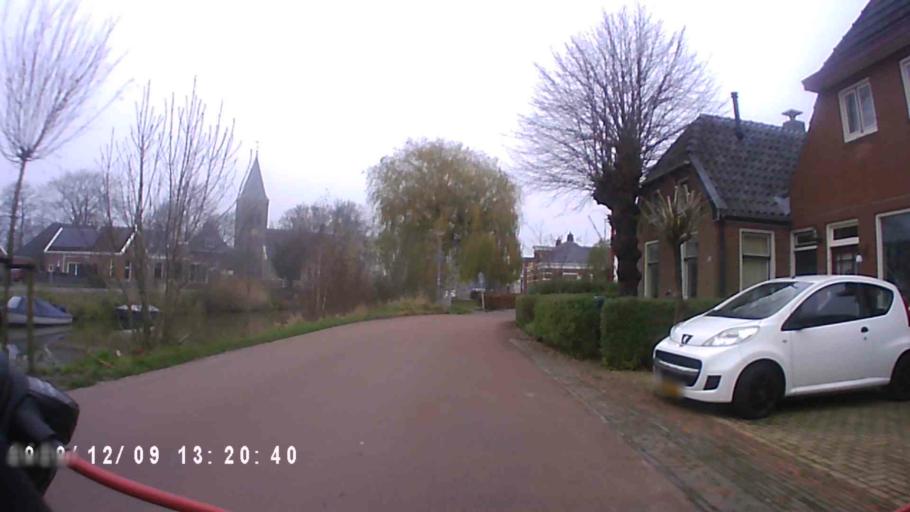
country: NL
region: Groningen
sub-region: Gemeente Groningen
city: Korrewegwijk
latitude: 53.2602
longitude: 6.5924
